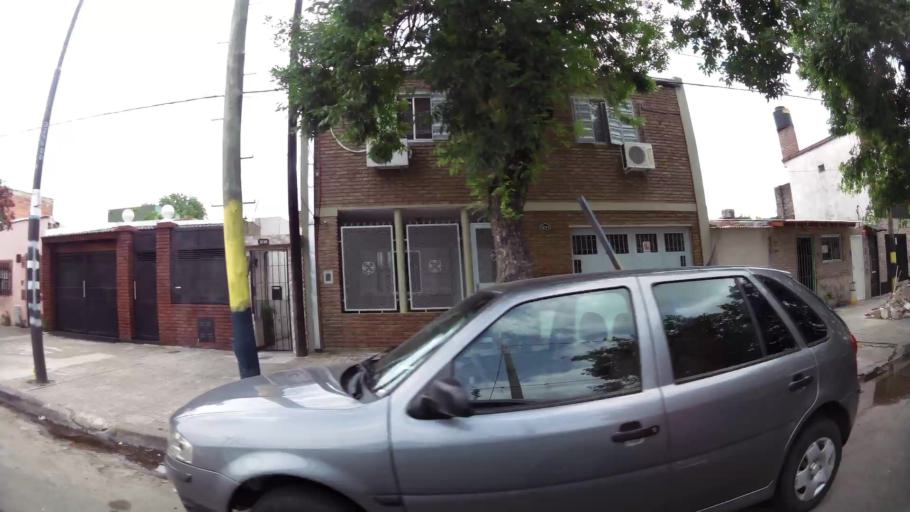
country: AR
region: Santa Fe
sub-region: Departamento de Rosario
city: Rosario
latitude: -32.9736
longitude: -60.6537
